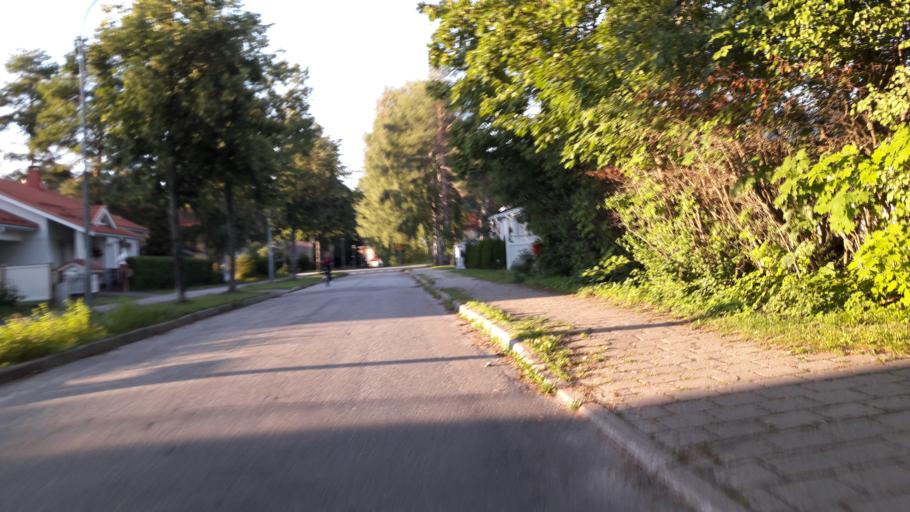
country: FI
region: North Karelia
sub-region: Joensuu
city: Joensuu
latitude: 62.6084
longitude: 29.7587
